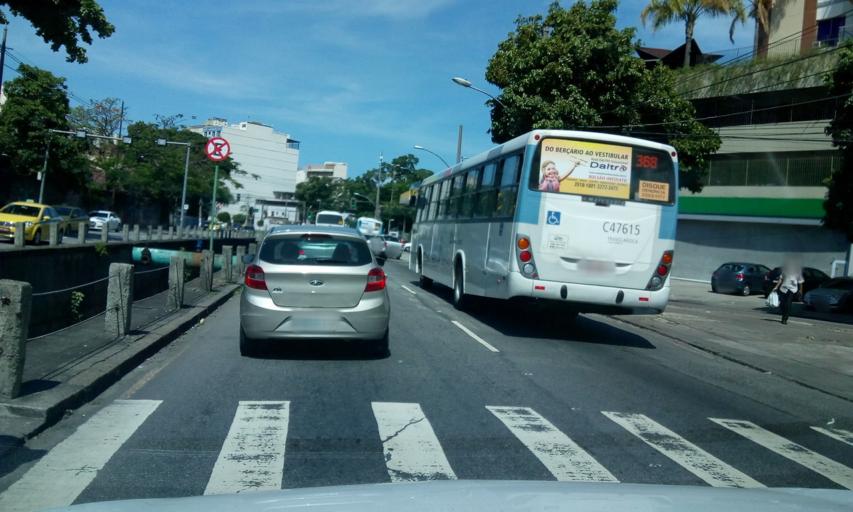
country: BR
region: Rio de Janeiro
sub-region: Rio De Janeiro
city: Rio de Janeiro
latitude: -22.9159
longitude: -43.2364
